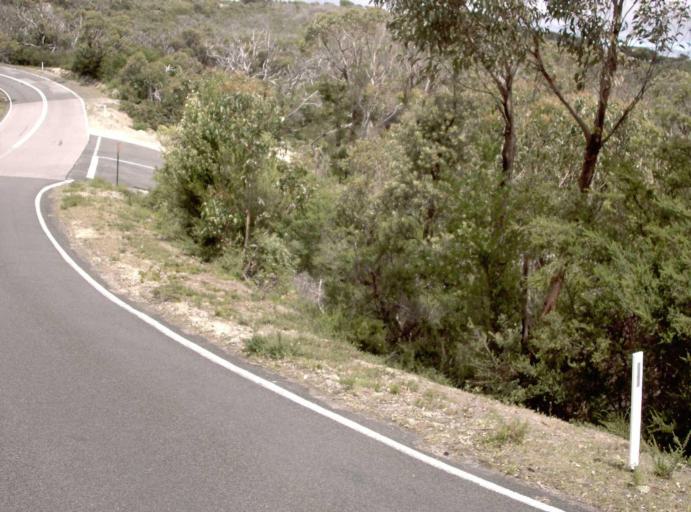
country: AU
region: Victoria
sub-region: Latrobe
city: Morwell
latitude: -39.0111
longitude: 146.2980
